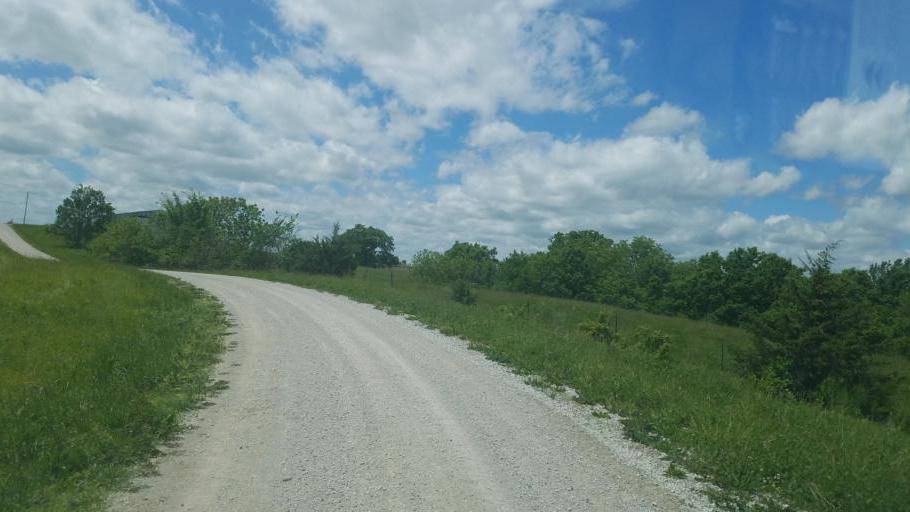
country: US
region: Iowa
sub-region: Decatur County
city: Lamoni
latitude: 40.5076
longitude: -94.0182
